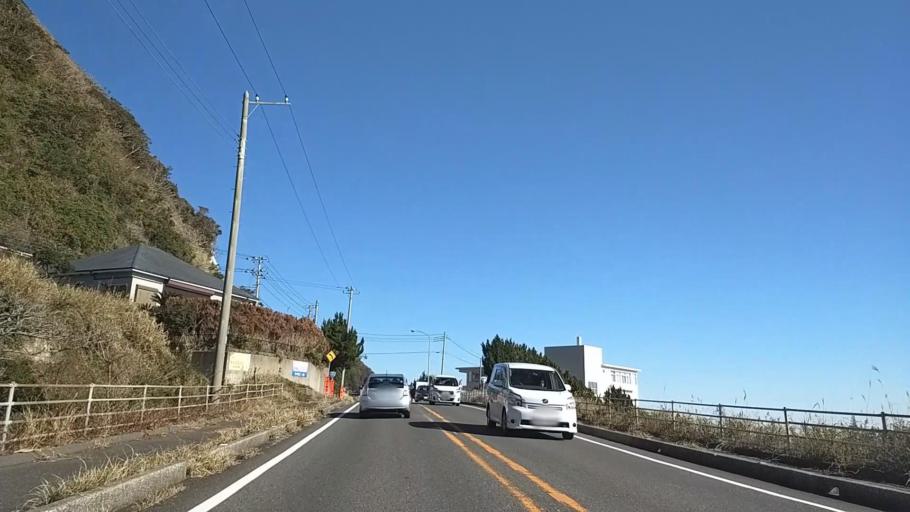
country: JP
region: Chiba
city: Kawaguchi
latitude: 35.0748
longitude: 140.0922
